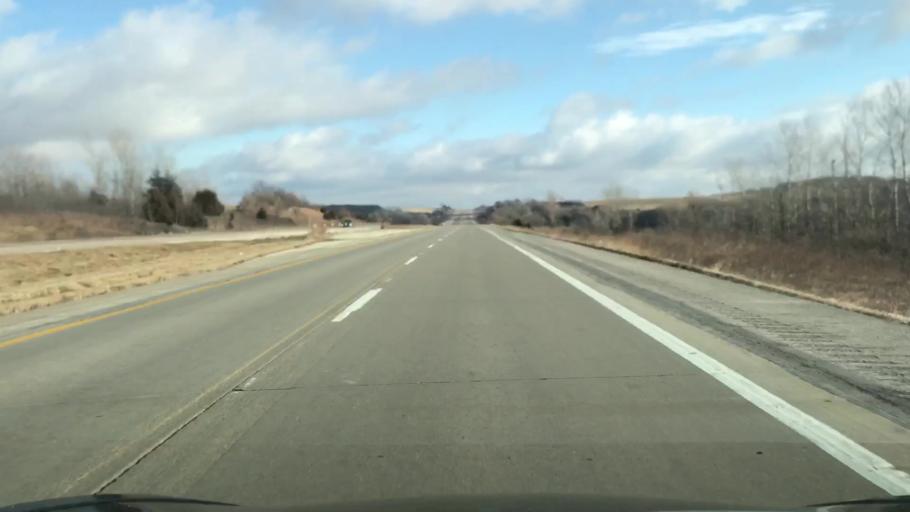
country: US
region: Iowa
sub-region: Cass County
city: Atlantic
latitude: 41.4971
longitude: -94.8504
